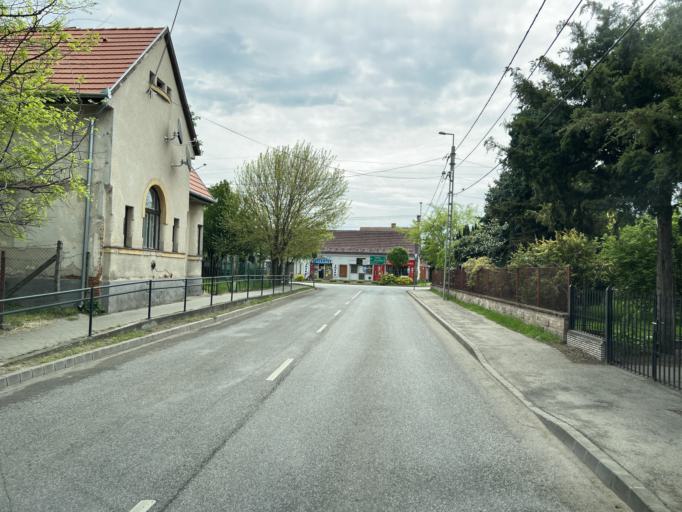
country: HU
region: Pest
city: Abony
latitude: 47.1876
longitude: 20.0031
